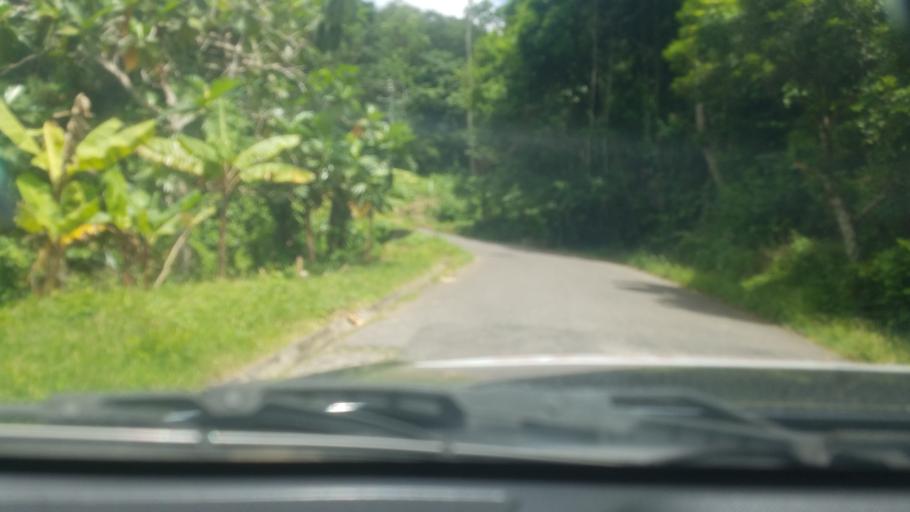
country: LC
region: Laborie Quarter
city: Laborie
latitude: 13.7936
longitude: -60.9542
